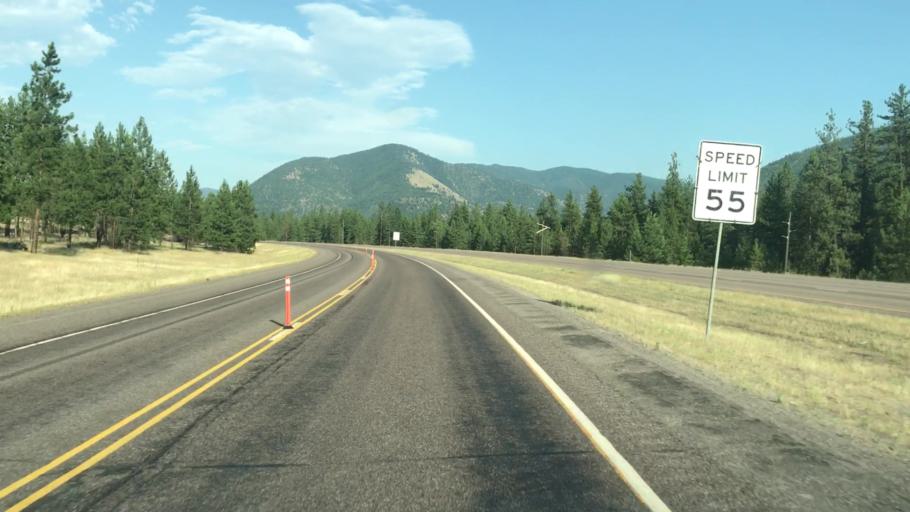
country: US
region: Montana
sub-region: Mineral County
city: Superior
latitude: 47.0123
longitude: -114.7245
